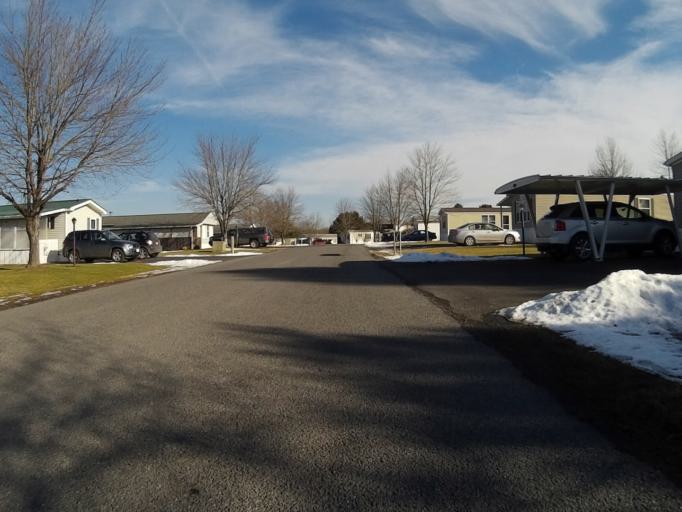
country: US
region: Pennsylvania
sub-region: Centre County
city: Houserville
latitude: 40.8719
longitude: -77.8663
